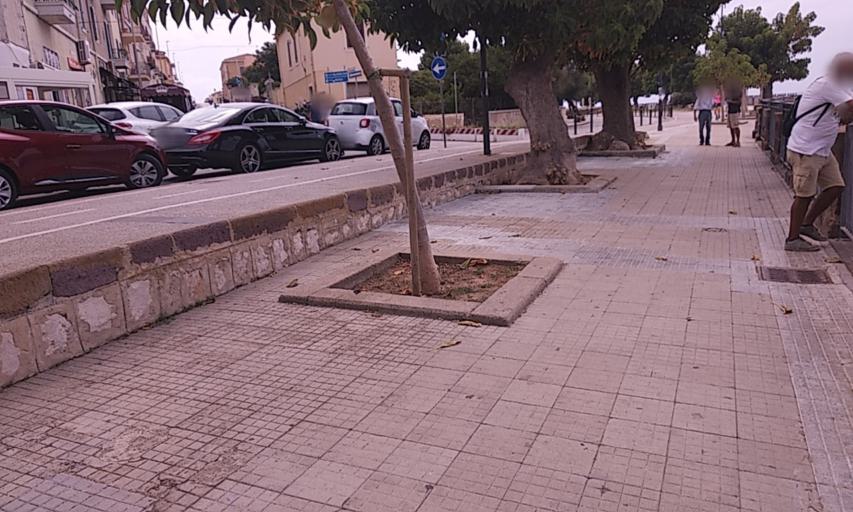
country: IT
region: Sardinia
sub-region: Provincia di Sassari
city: Alghero
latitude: 40.5554
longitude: 8.3159
